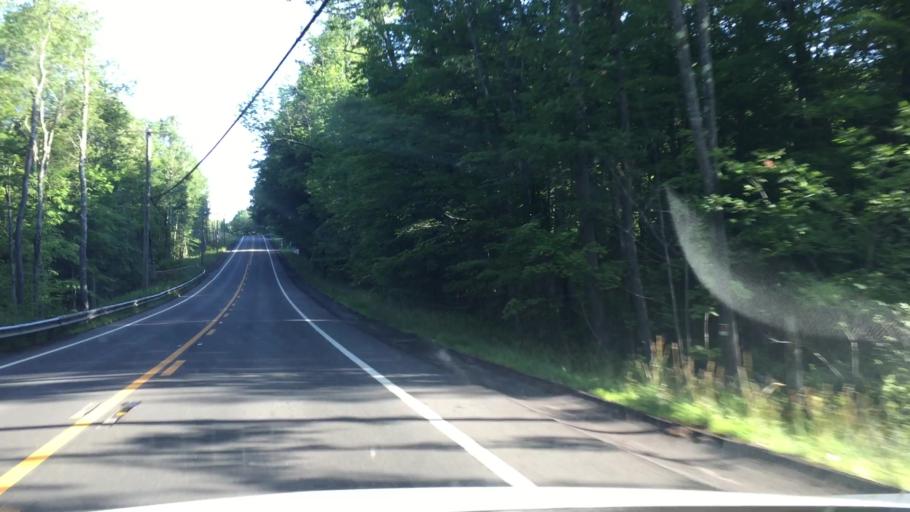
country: US
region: Massachusetts
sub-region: Berkshire County
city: Becket
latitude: 42.2703
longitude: -73.0534
